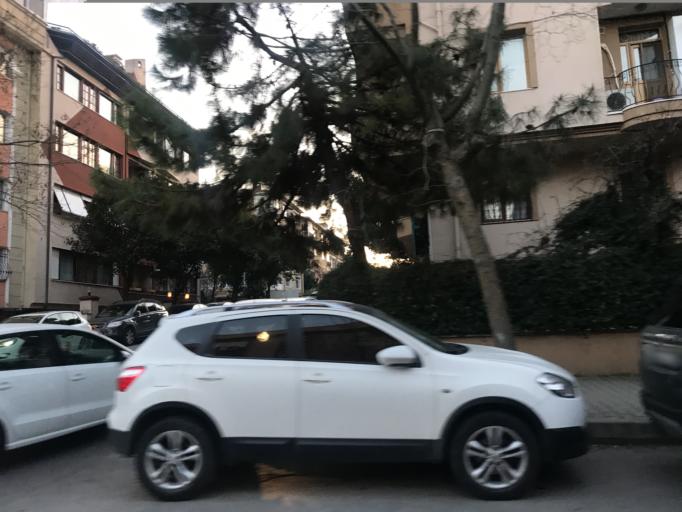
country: TR
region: Istanbul
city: Bahcelievler
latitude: 40.9600
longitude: 28.8193
